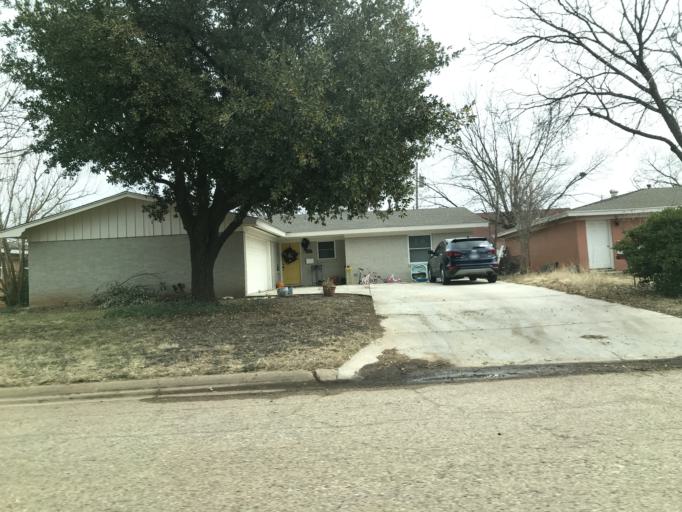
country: US
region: Texas
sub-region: Taylor County
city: Abilene
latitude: 32.4712
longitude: -99.7621
